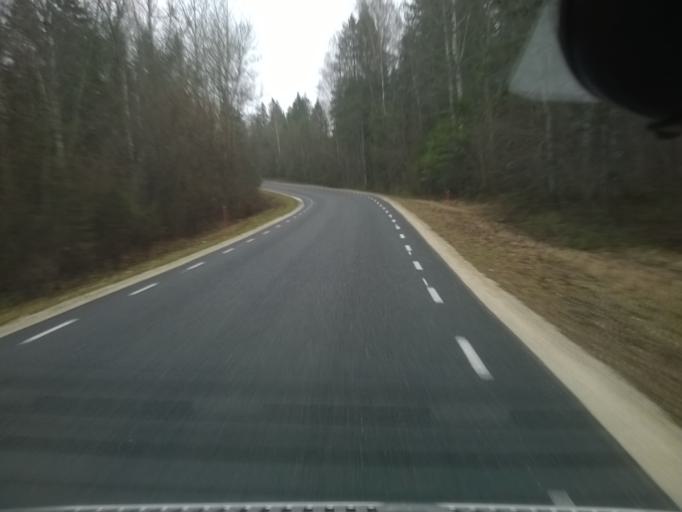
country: EE
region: Harju
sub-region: Saue linn
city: Saue
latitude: 59.1406
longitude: 24.5180
